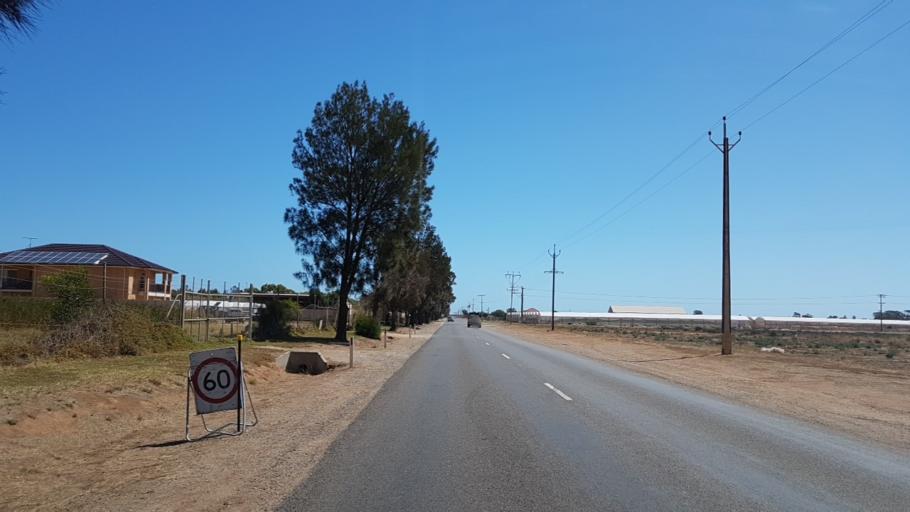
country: AU
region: South Australia
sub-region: Playford
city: Virginia
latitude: -34.7280
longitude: 138.5660
